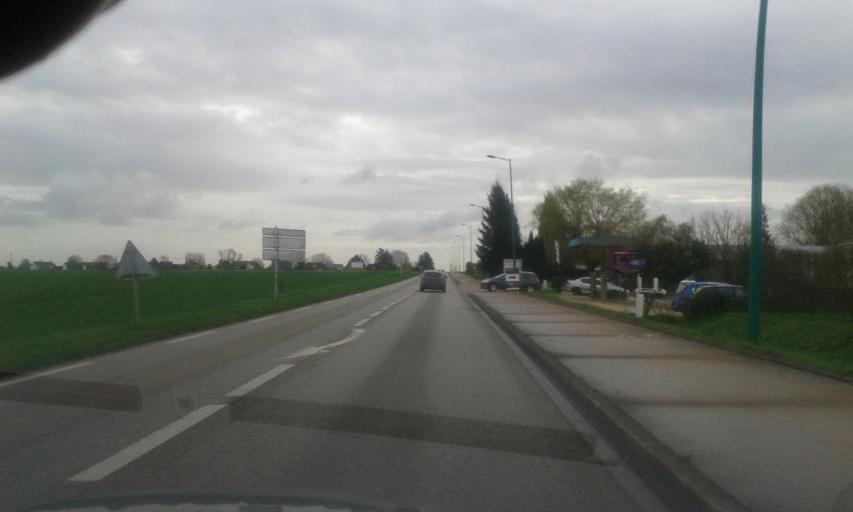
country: FR
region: Haute-Normandie
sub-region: Departement de la Seine-Maritime
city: Boos
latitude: 49.3879
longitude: 1.2127
